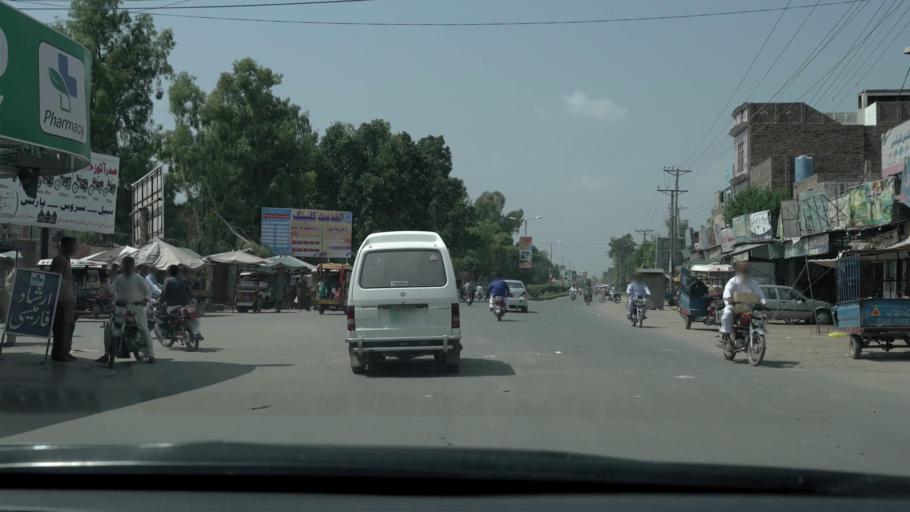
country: PK
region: Punjab
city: Gojra
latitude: 31.1527
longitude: 72.6743
